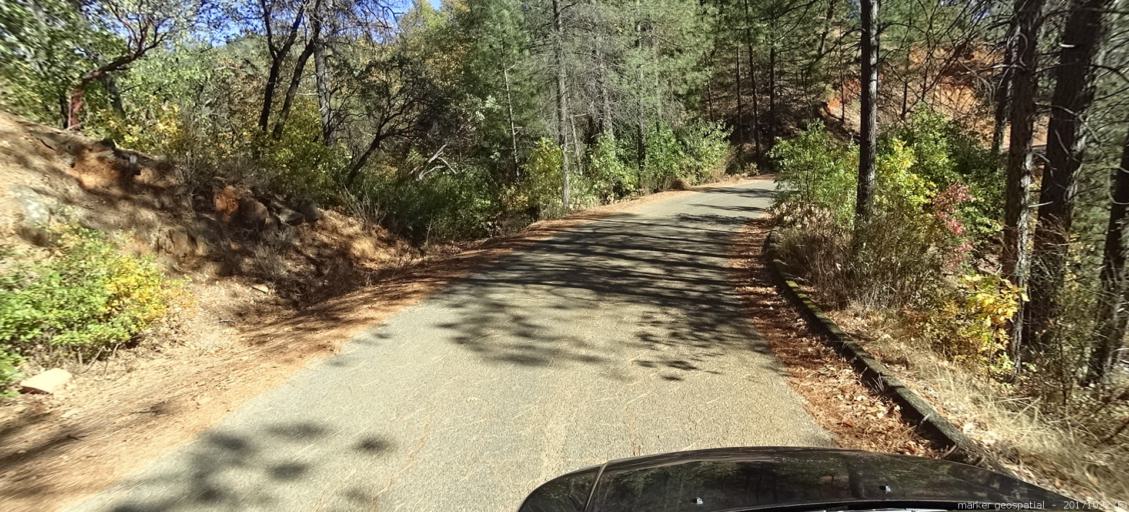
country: US
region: California
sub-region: Shasta County
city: Shasta Lake
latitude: 40.8818
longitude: -122.3674
